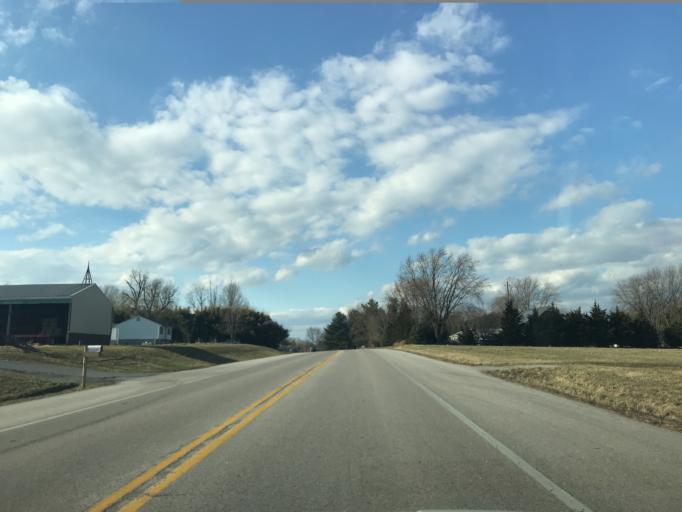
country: US
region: Maryland
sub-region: Cecil County
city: Rising Sun
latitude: 39.6659
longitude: -76.0154
